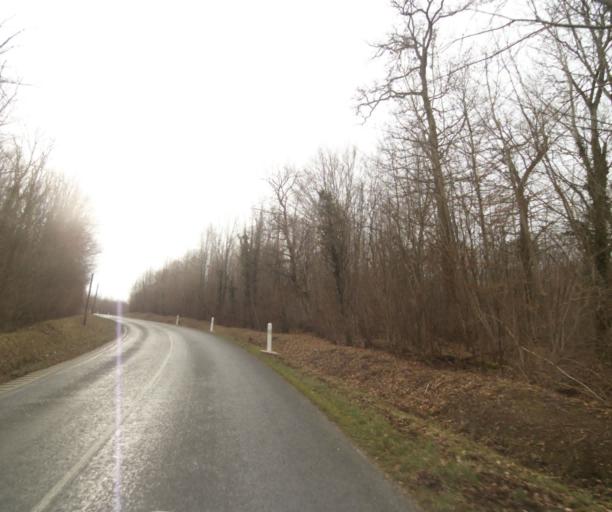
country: FR
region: Champagne-Ardenne
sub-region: Departement de la Haute-Marne
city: Villiers-en-Lieu
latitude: 48.6952
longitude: 4.8927
